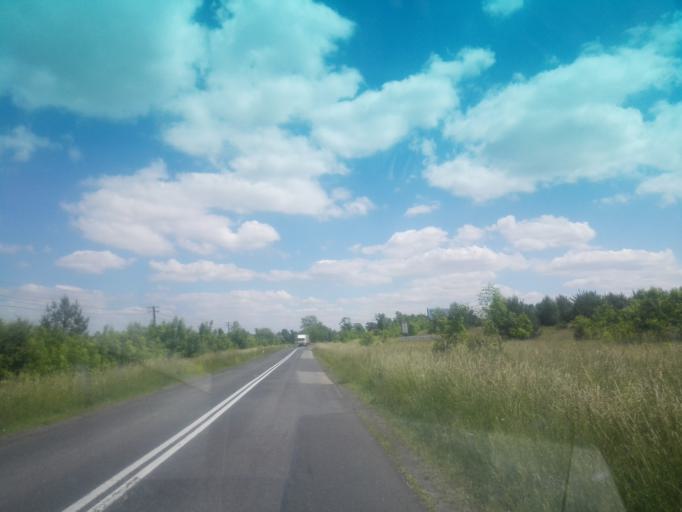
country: PL
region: Silesian Voivodeship
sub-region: Powiat czestochowski
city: Potok Zloty
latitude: 50.7362
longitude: 19.3899
